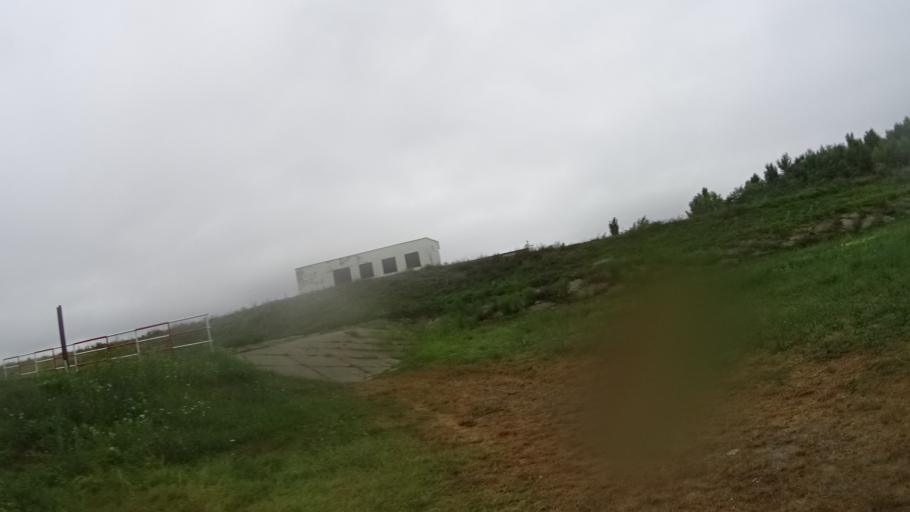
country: HU
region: Komarom-Esztergom
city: Labatlan
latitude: 47.7604
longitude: 18.5237
